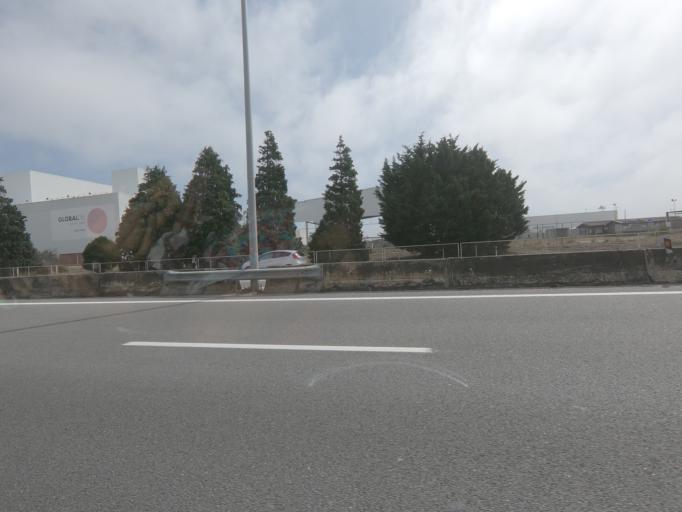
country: PT
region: Porto
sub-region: Matosinhos
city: Santa Cruz do Bispo
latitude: 41.2130
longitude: -8.6906
